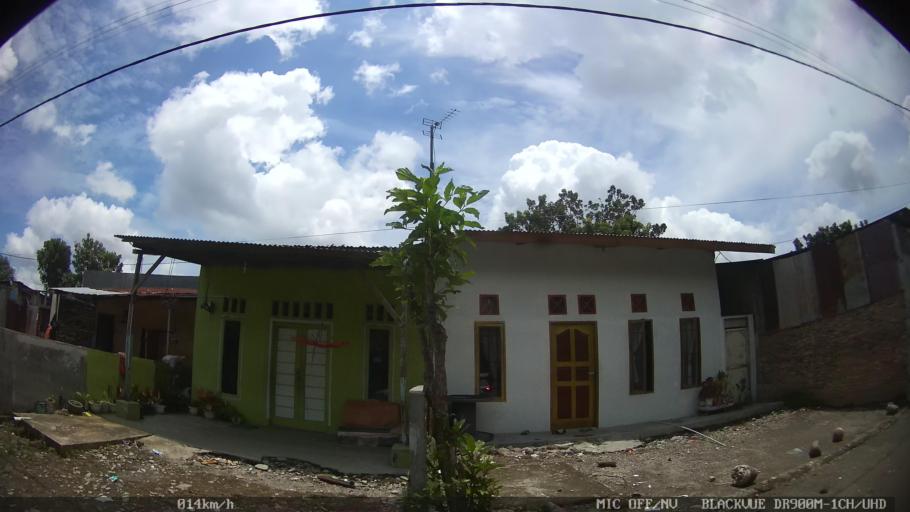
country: ID
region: North Sumatra
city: Medan
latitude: 3.6099
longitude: 98.7217
